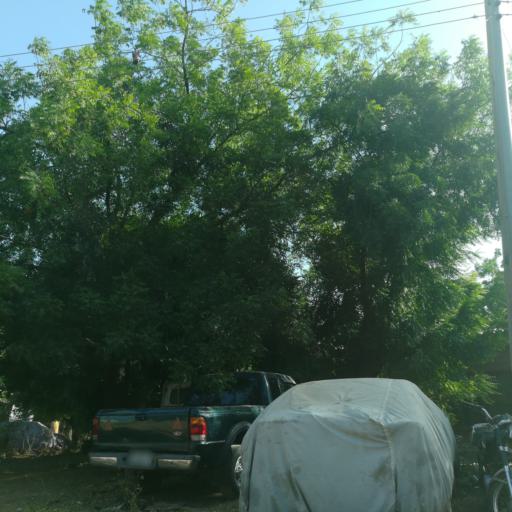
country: NG
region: Kano
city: Kano
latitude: 12.0184
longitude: 8.5036
